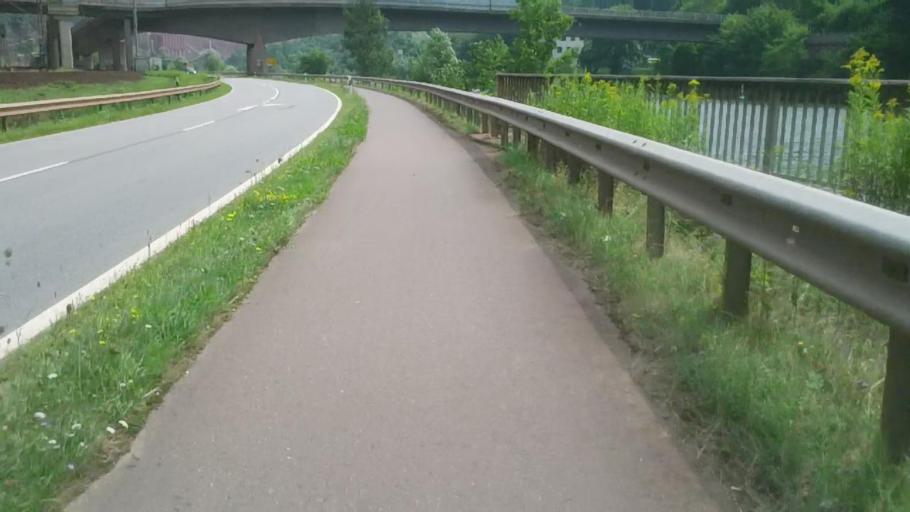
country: DE
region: Rheinland-Pfalz
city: Taben-Rodt
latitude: 49.5536
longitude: 6.5982
